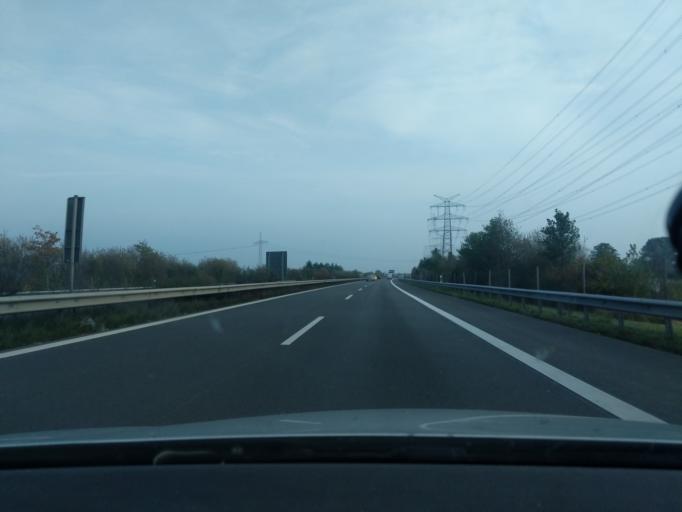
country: DE
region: Lower Saxony
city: Agathenburg
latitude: 53.5772
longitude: 9.5300
